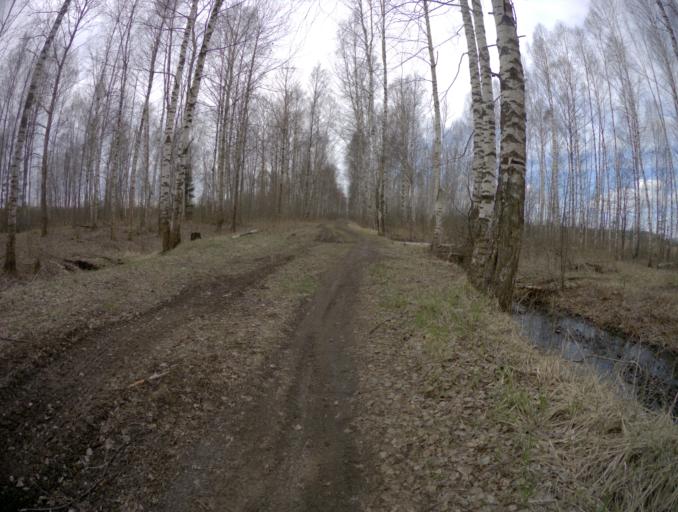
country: RU
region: Vladimir
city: Raduzhnyy
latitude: 55.9108
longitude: 40.2361
